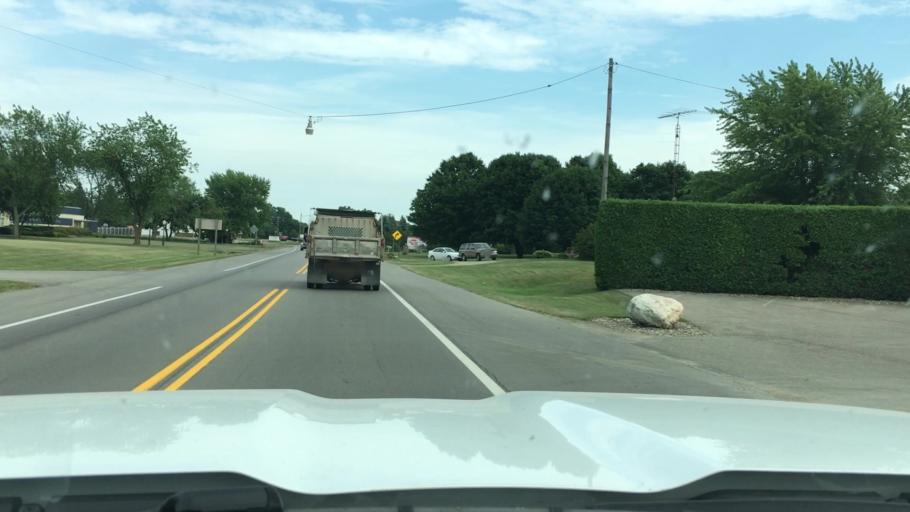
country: US
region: Michigan
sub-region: Sanilac County
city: Marlette
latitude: 43.3368
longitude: -83.0830
